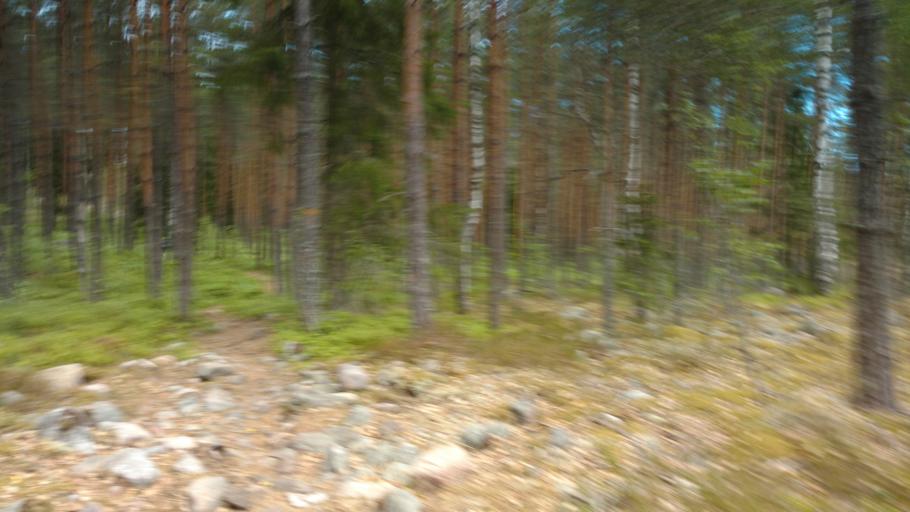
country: FI
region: Uusimaa
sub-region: Raaseporin
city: Pohja
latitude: 60.1139
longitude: 23.5681
